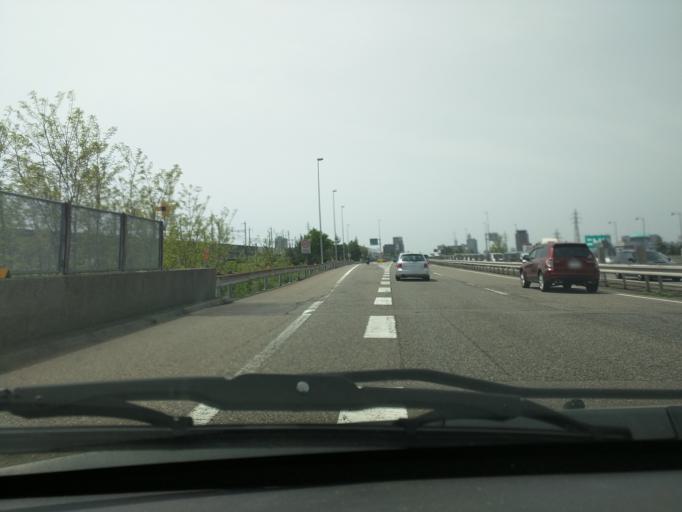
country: JP
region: Niigata
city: Tsubame
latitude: 37.6549
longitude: 138.9413
